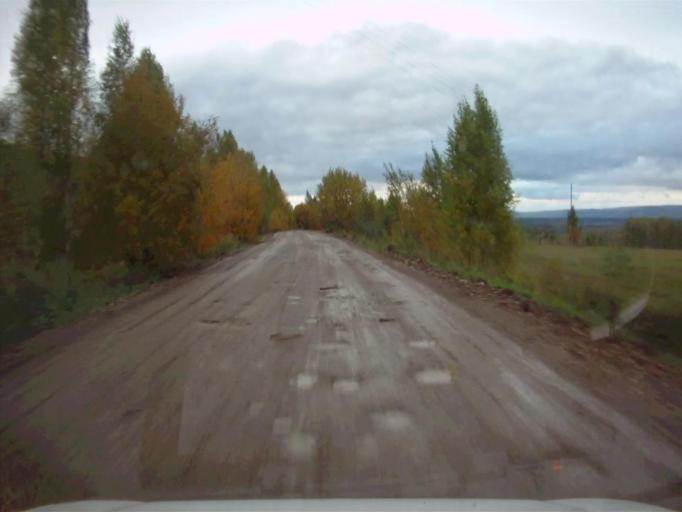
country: RU
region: Sverdlovsk
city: Mikhaylovsk
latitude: 56.2004
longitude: 59.2003
